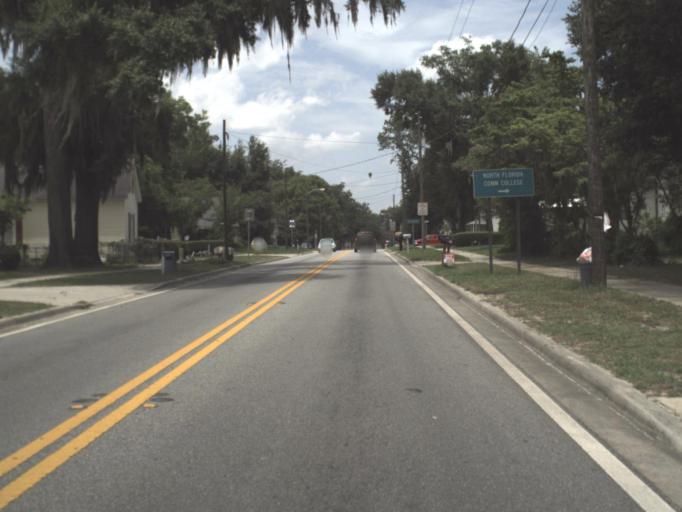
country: US
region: Florida
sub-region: Madison County
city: Madison
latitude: 30.4613
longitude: -83.4132
